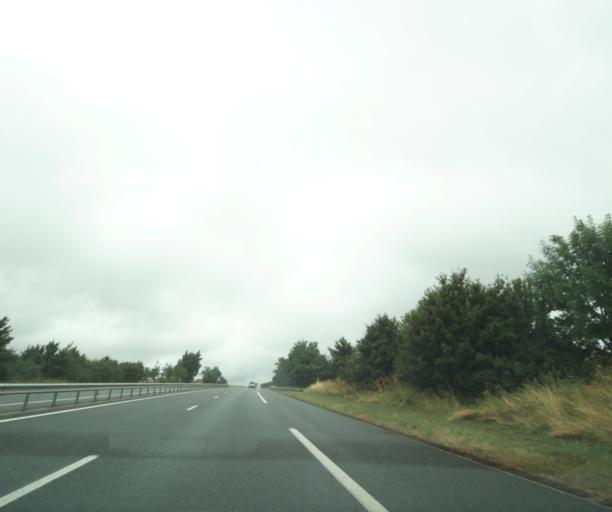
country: FR
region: Midi-Pyrenees
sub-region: Departement de l'Aveyron
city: Luc-la-Primaube
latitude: 44.3058
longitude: 2.5330
